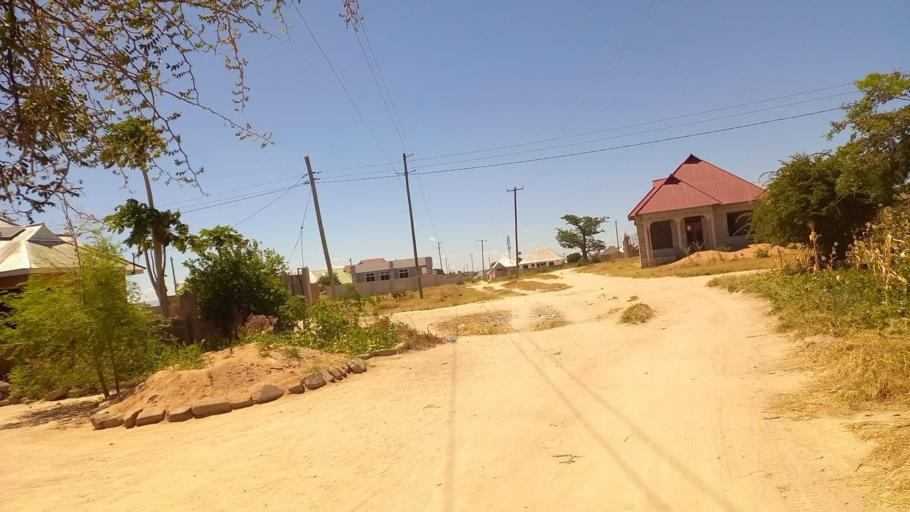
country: TZ
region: Dodoma
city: Dodoma
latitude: -6.1342
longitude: 35.7145
